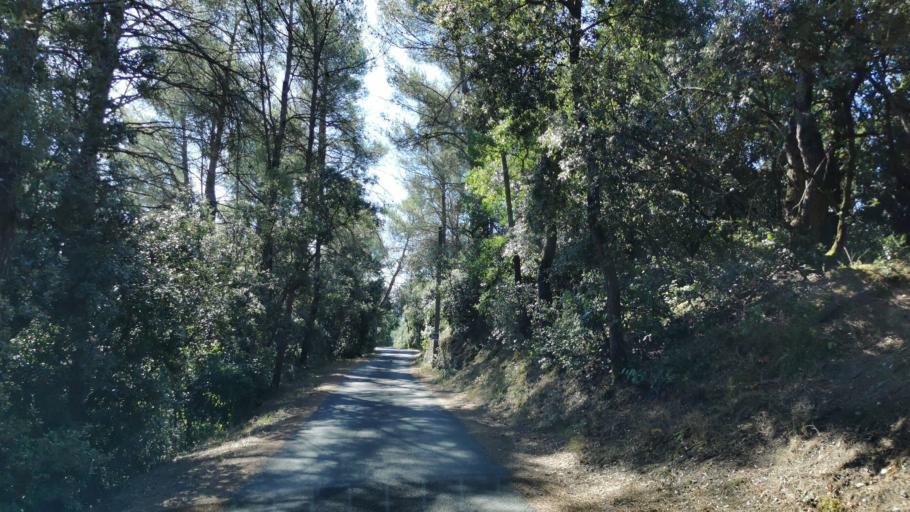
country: FR
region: Languedoc-Roussillon
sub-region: Departement de l'Aude
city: Conques-sur-Orbiel
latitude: 43.2453
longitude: 2.4112
